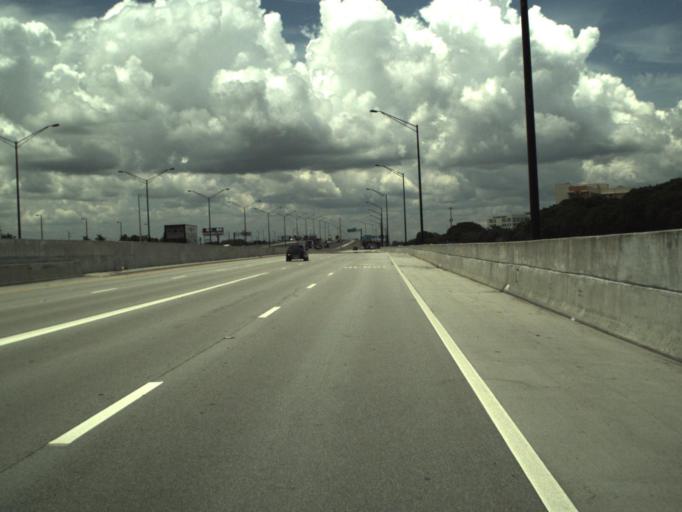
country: US
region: Florida
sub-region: Broward County
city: Pine Island Ridge
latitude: 26.1013
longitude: -80.2572
